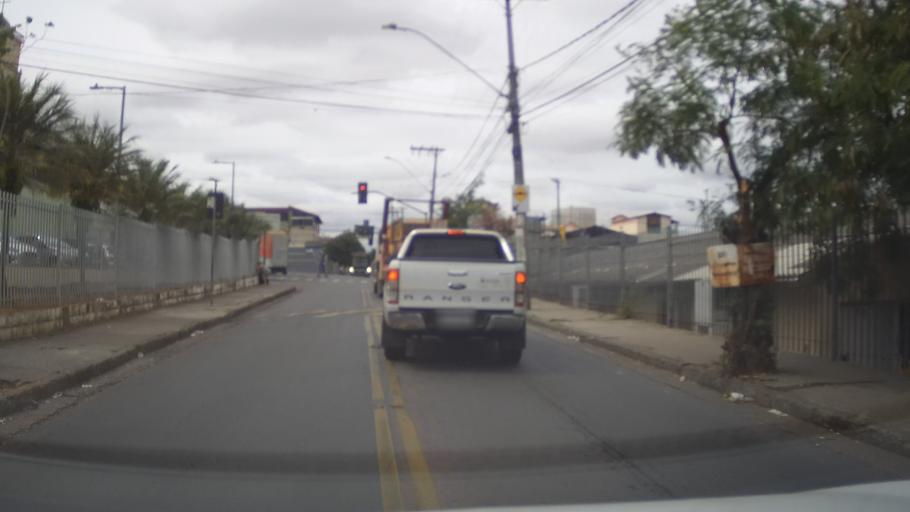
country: BR
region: Minas Gerais
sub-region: Belo Horizonte
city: Belo Horizonte
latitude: -19.8666
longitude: -43.9257
